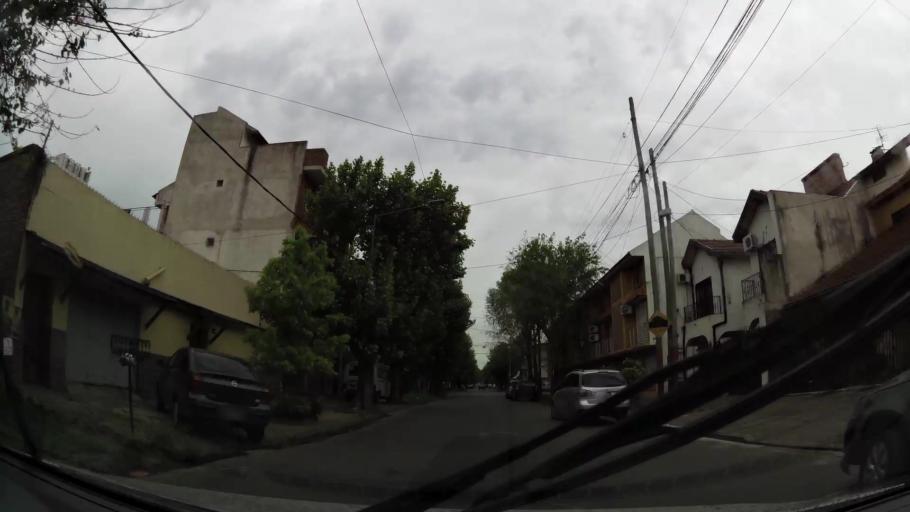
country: AR
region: Buenos Aires
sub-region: Partido de Lanus
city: Lanus
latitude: -34.7031
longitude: -58.3991
